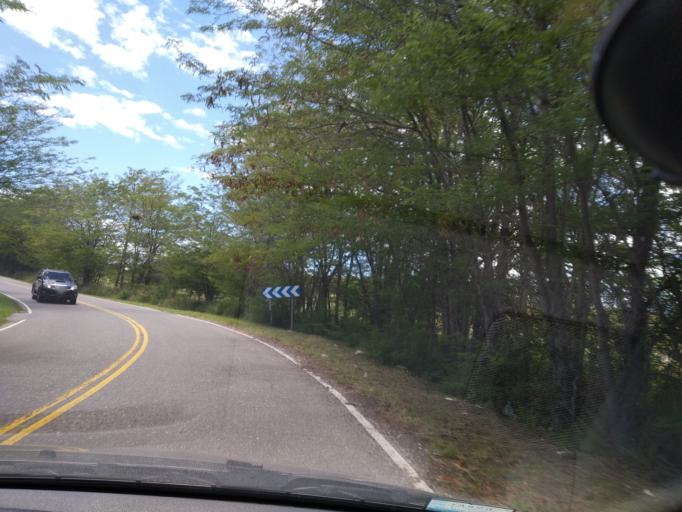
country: AR
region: Cordoba
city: Cuesta Blanca
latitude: -31.5976
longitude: -64.5646
